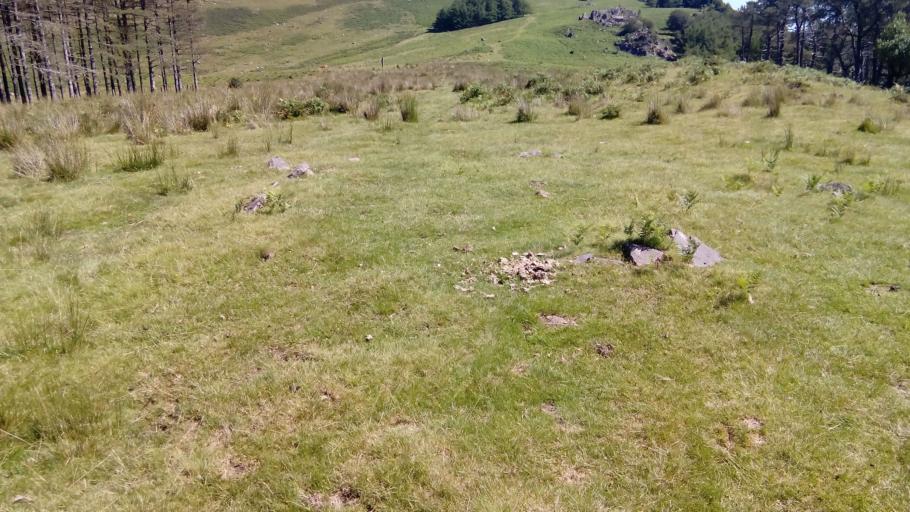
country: ES
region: Basque Country
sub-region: Provincia de Guipuzcoa
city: Urnieta
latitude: 43.1985
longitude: -1.9649
